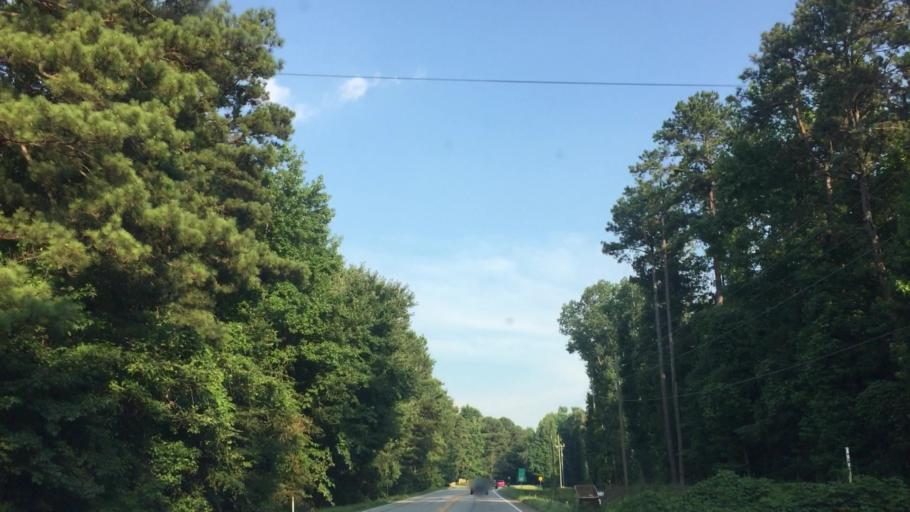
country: US
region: Georgia
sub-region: DeKalb County
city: Pine Mountain
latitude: 33.6249
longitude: -84.1763
